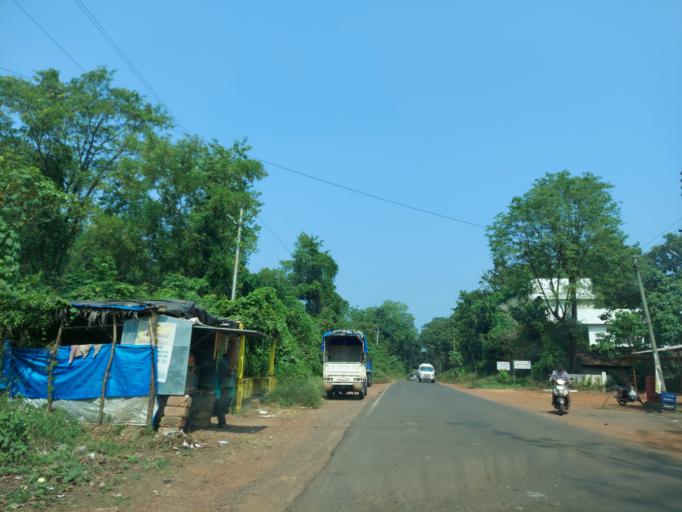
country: IN
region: Maharashtra
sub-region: Sindhudurg
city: Kudal
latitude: 15.9913
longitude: 73.6838
